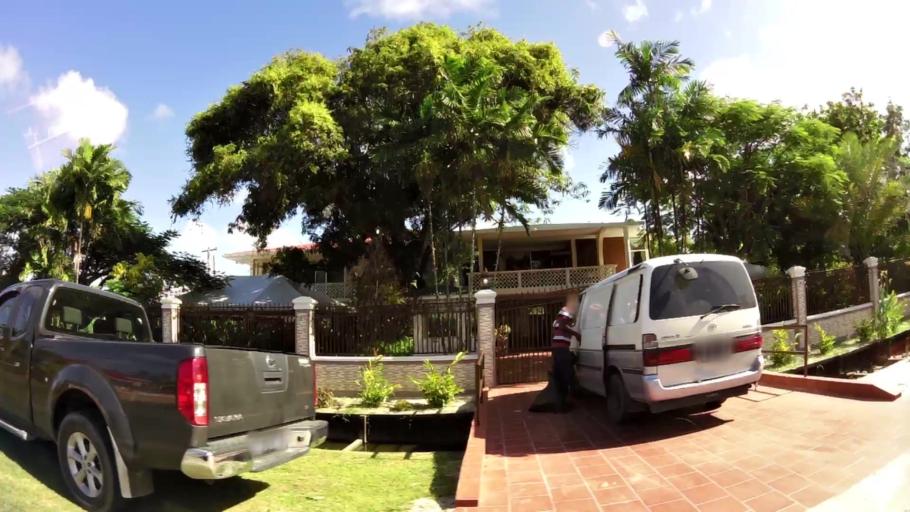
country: GY
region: Demerara-Mahaica
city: Georgetown
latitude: 6.8210
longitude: -58.1288
